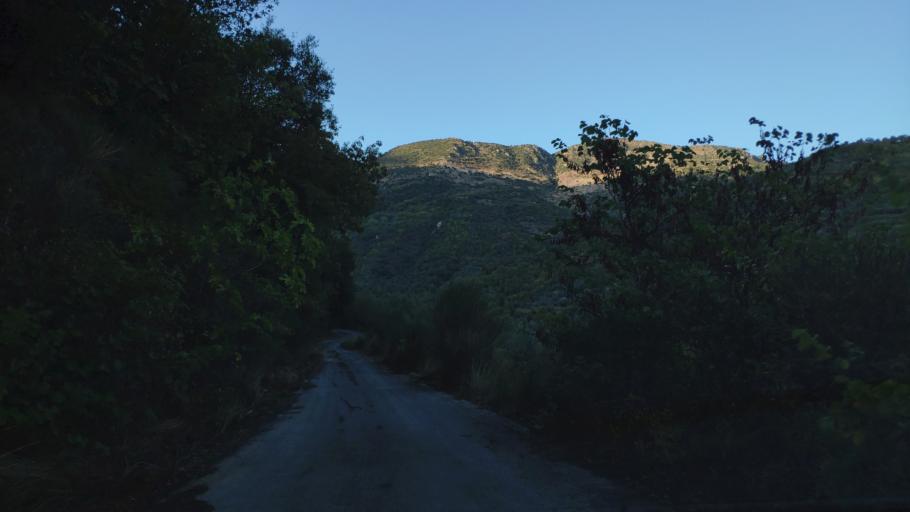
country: GR
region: Peloponnese
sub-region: Nomos Arkadias
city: Dimitsana
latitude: 37.5672
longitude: 22.0420
